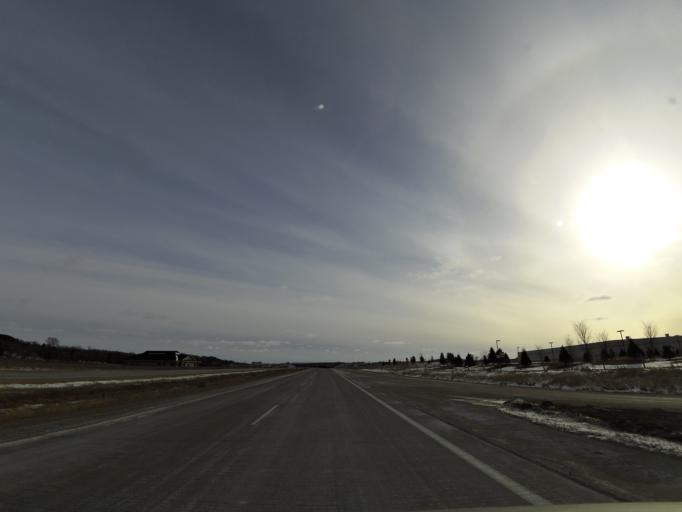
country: US
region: Wisconsin
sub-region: Saint Croix County
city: Hudson
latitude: 44.9468
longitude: -92.6952
